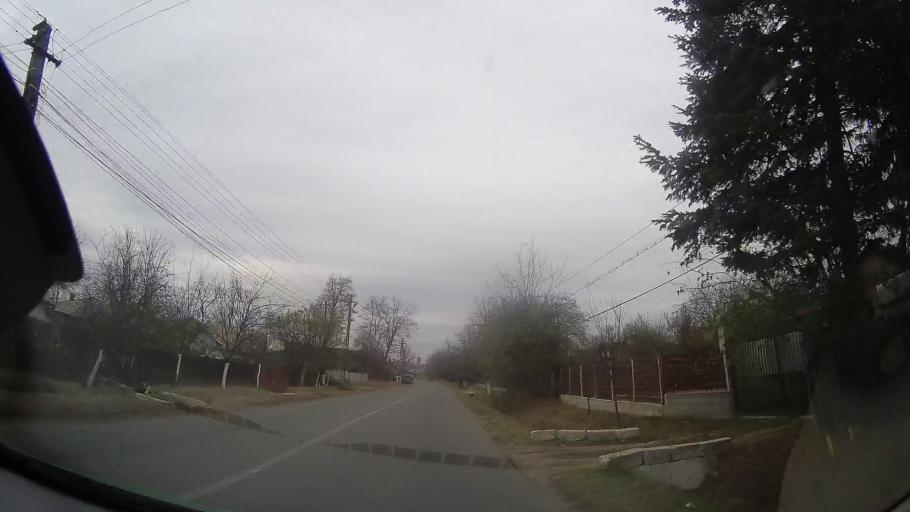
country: RO
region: Prahova
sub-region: Comuna Iordachianu
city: Iordacheanu
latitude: 45.0524
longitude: 26.2393
